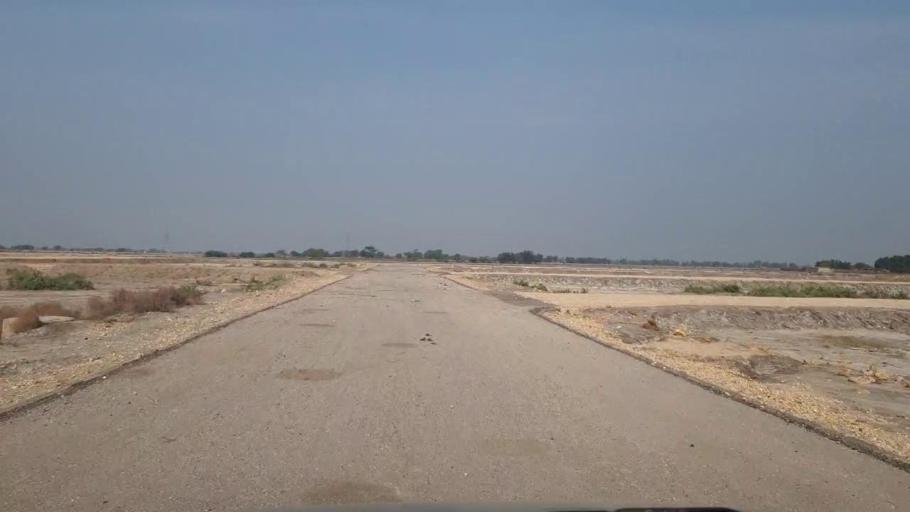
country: PK
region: Sindh
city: Tando Muhammad Khan
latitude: 25.1336
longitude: 68.5190
